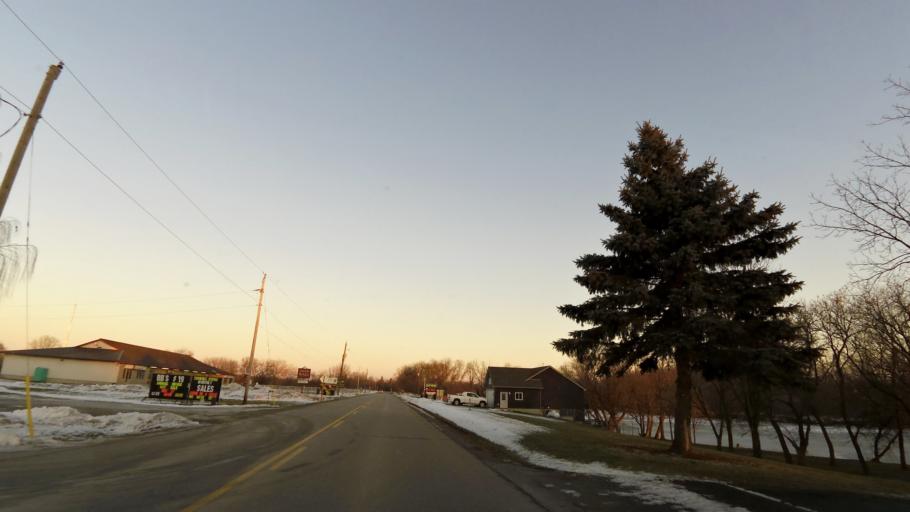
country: CA
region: Ontario
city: Ancaster
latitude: 43.1004
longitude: -80.0829
